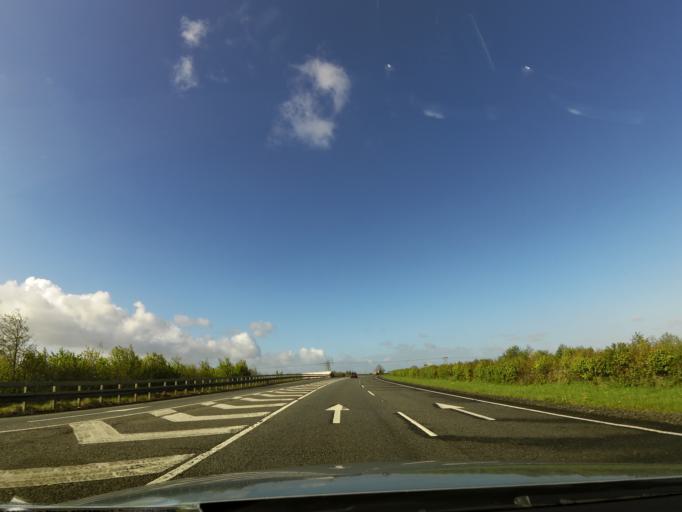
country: IE
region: Munster
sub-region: County Limerick
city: Annacotty
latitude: 52.6453
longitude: -8.5659
